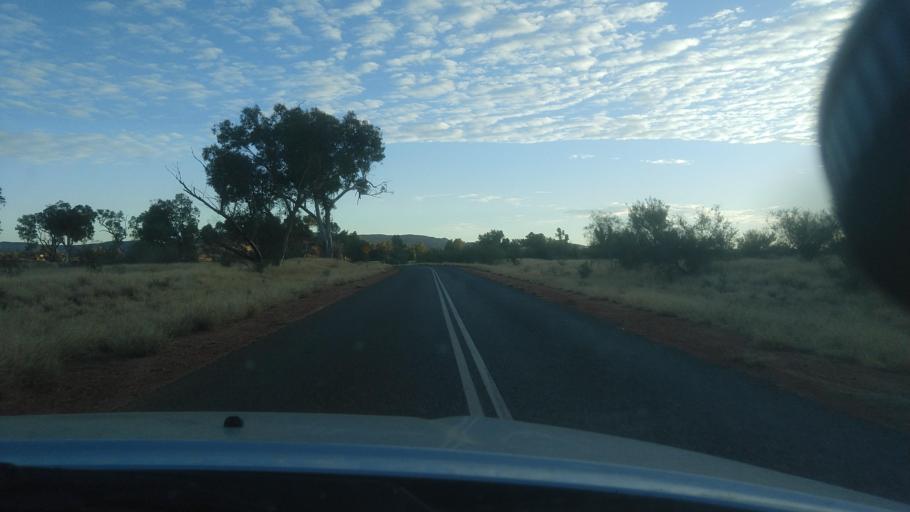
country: AU
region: Northern Territory
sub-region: Alice Springs
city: Alice Springs
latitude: -23.7378
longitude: 133.7418
